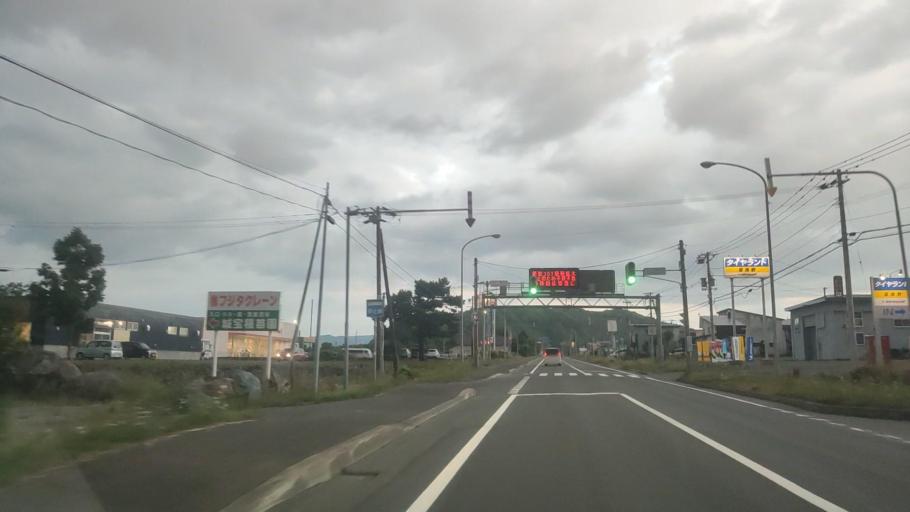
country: JP
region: Hokkaido
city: Shimo-furano
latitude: 43.3495
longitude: 142.3674
